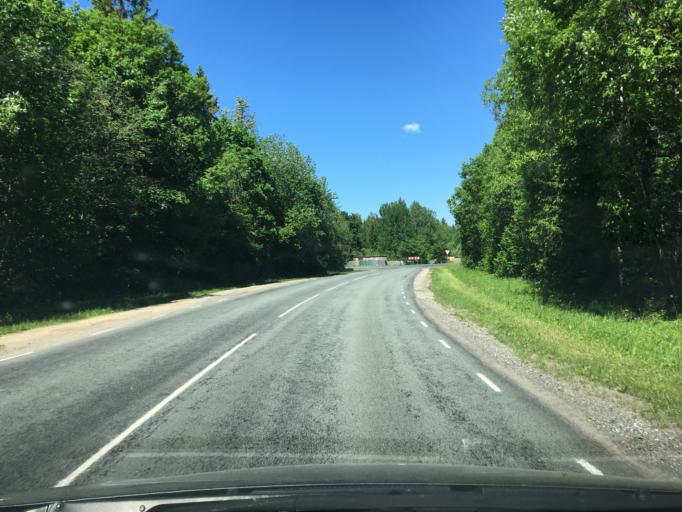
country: EE
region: Harju
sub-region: Rae vald
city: Vaida
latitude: 59.2062
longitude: 24.9420
